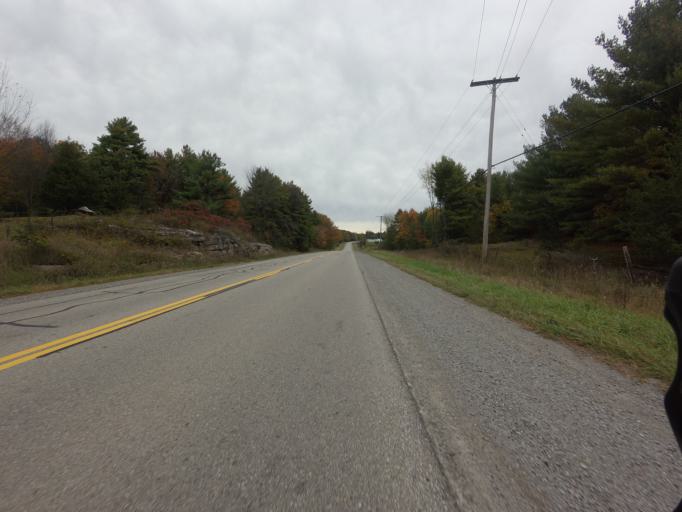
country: CA
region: Ontario
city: Gananoque
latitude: 44.5575
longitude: -76.1181
